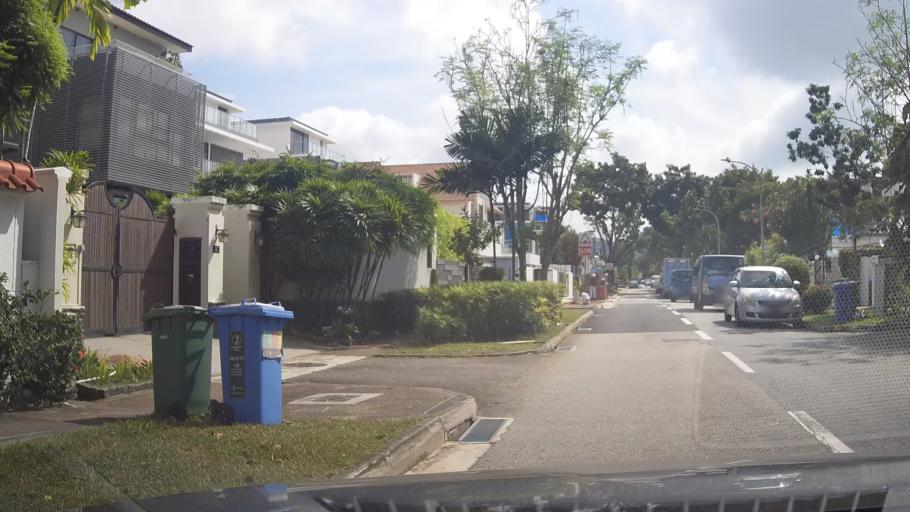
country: SG
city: Singapore
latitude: 1.3028
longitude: 103.8922
